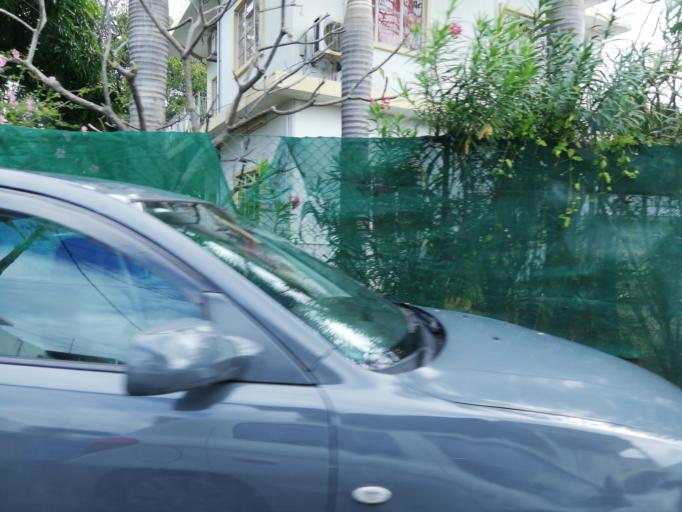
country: MU
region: Port Louis
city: Port Louis
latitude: -20.1633
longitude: 57.4877
